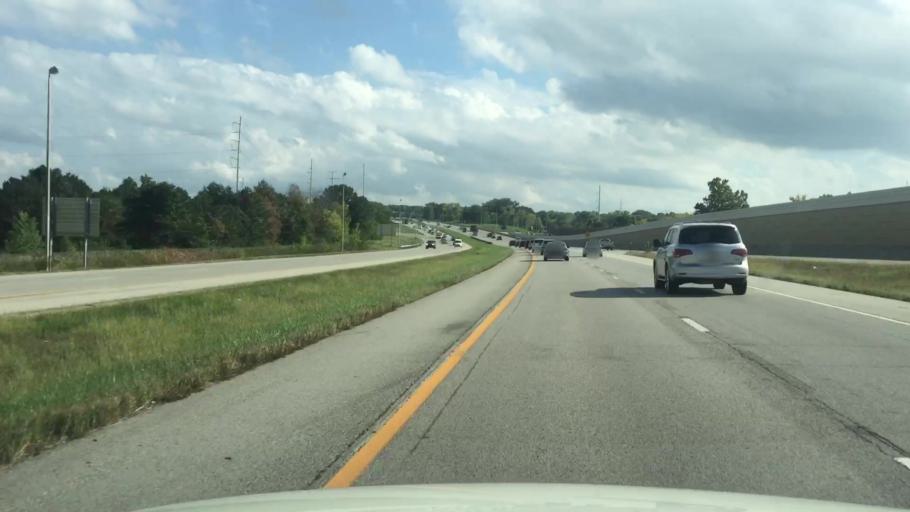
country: US
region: Kansas
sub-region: Johnson County
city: Lenexa
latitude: 38.9191
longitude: -94.7033
